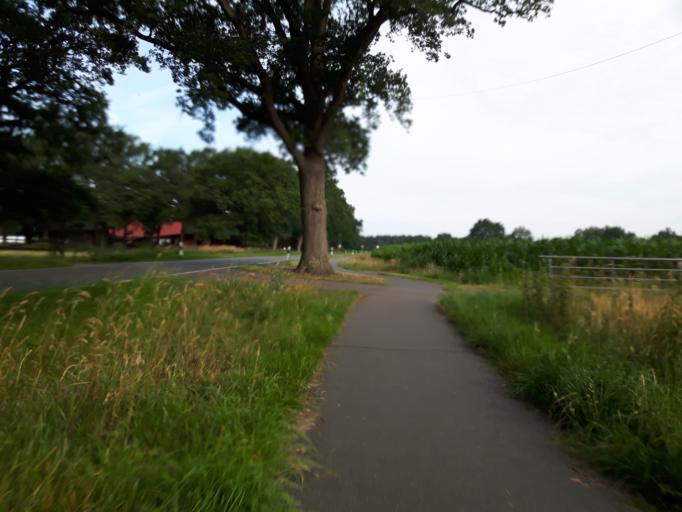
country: DE
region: Lower Saxony
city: Delmenhorst
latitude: 53.0984
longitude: 8.5931
